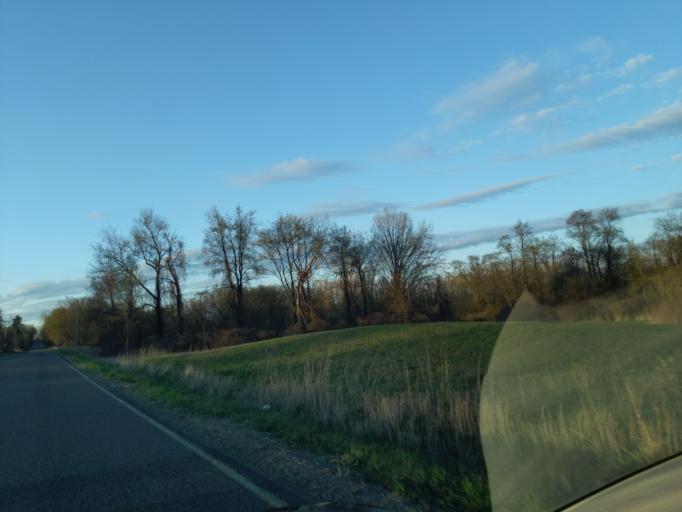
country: US
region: Michigan
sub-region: Ingham County
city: Leslie
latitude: 42.4273
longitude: -84.4431
